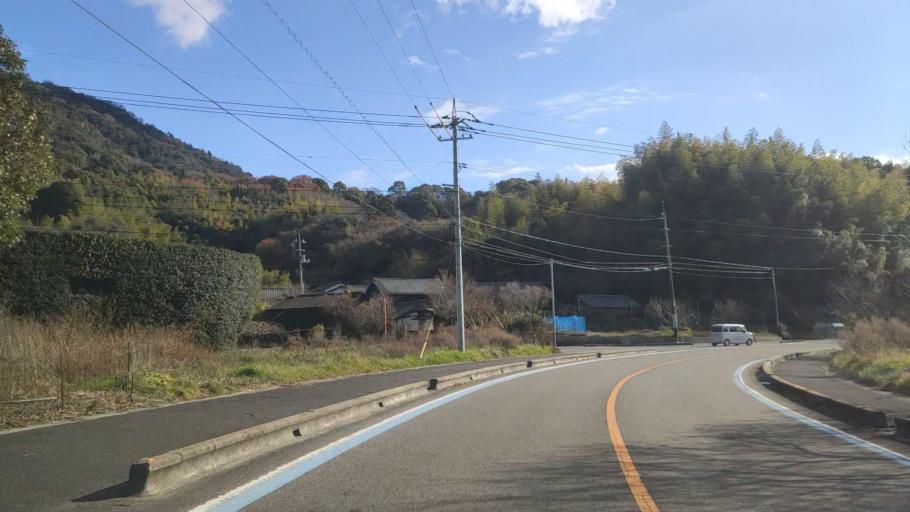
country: JP
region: Hiroshima
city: Innoshima
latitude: 34.2208
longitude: 133.0684
